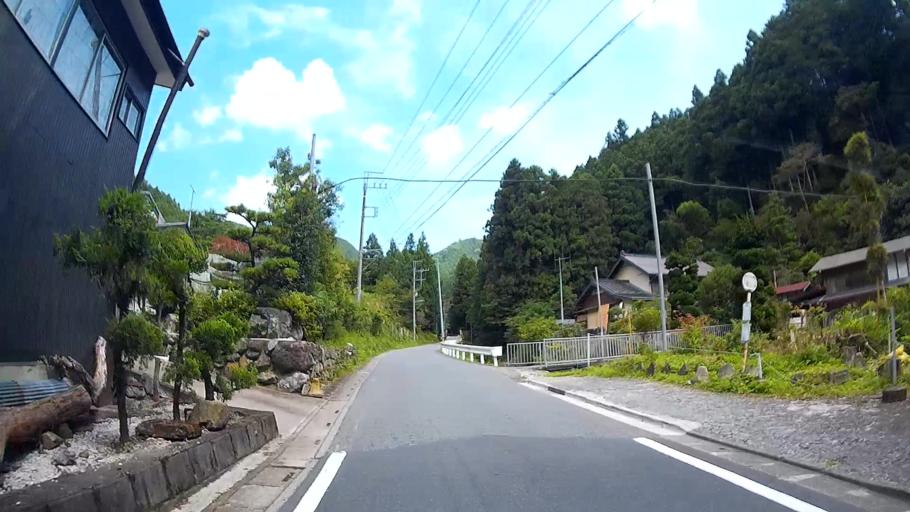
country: JP
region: Saitama
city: Chichibu
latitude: 35.9185
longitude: 139.1505
